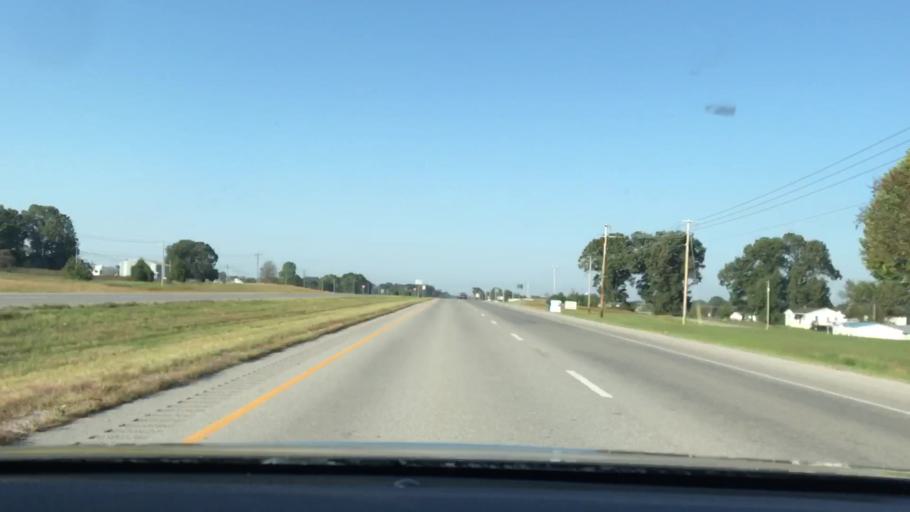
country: US
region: Kentucky
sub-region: Trigg County
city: Cadiz
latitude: 36.8757
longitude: -87.7533
